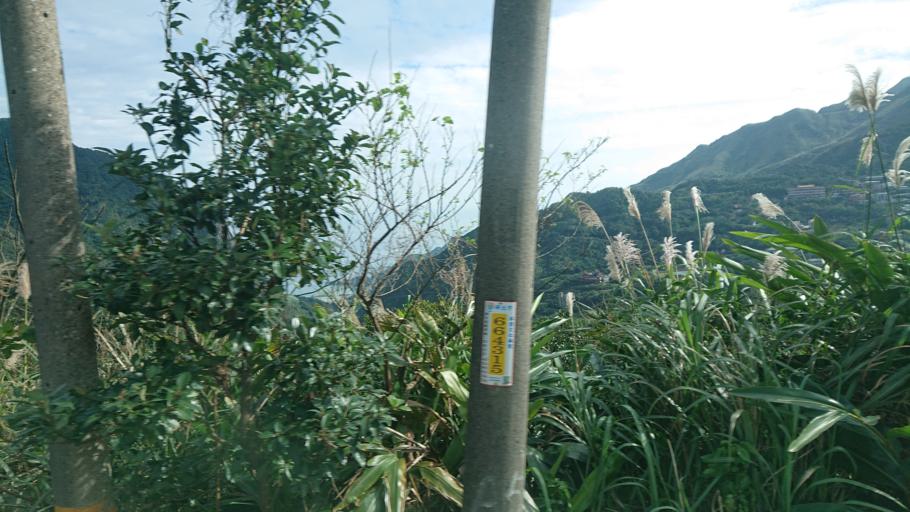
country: TW
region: Taiwan
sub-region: Keelung
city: Keelung
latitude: 25.1115
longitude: 121.8497
